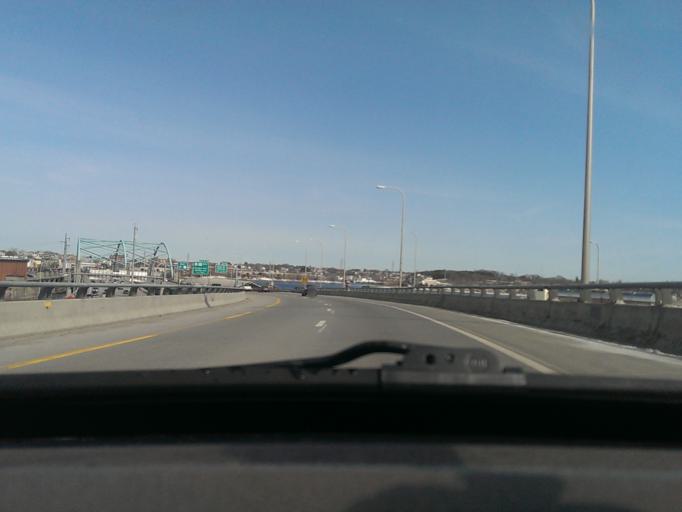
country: US
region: Rhode Island
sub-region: Providence County
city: Providence
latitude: 41.8135
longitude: -71.4062
